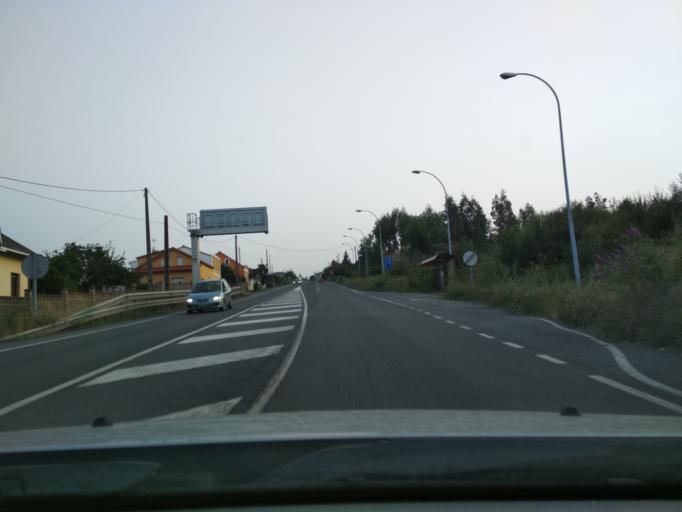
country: ES
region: Galicia
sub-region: Provincia da Coruna
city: Cambre
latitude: 43.2740
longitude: -8.3650
